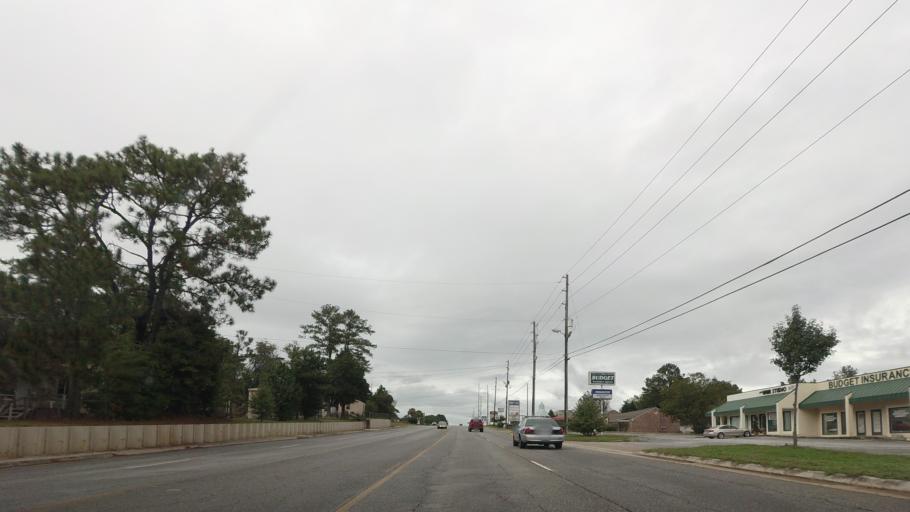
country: US
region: Georgia
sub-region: Houston County
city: Warner Robins
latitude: 32.5865
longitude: -83.6228
